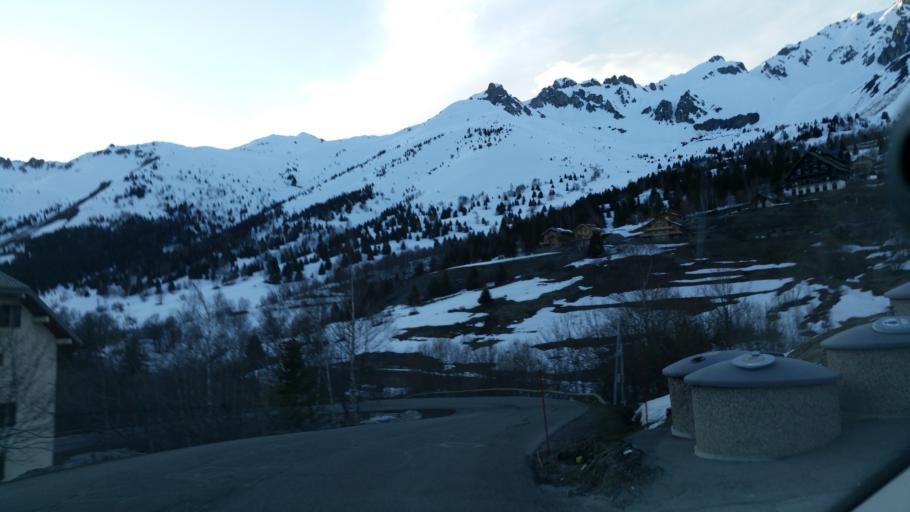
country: FR
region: Rhone-Alpes
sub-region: Departement de la Savoie
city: La Chambre
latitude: 45.4171
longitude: 6.3609
